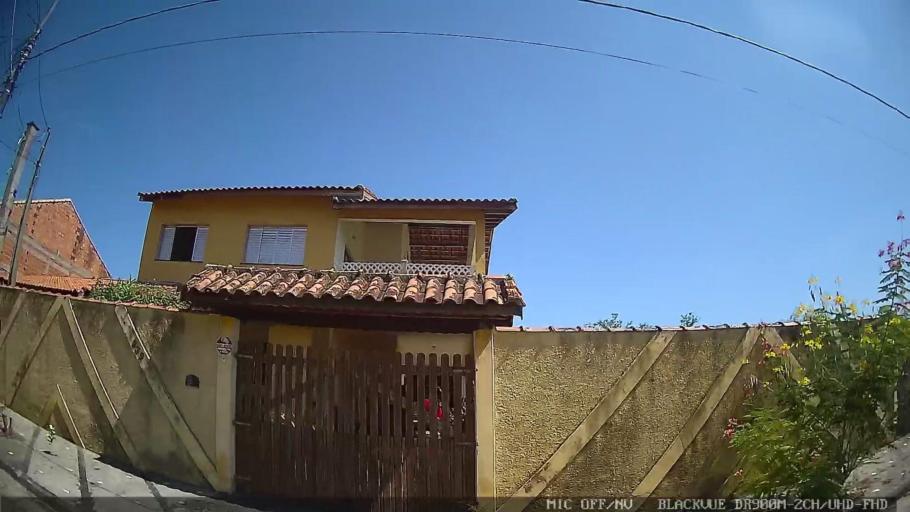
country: BR
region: Sao Paulo
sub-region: Peruibe
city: Peruibe
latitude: -24.2964
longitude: -46.9760
